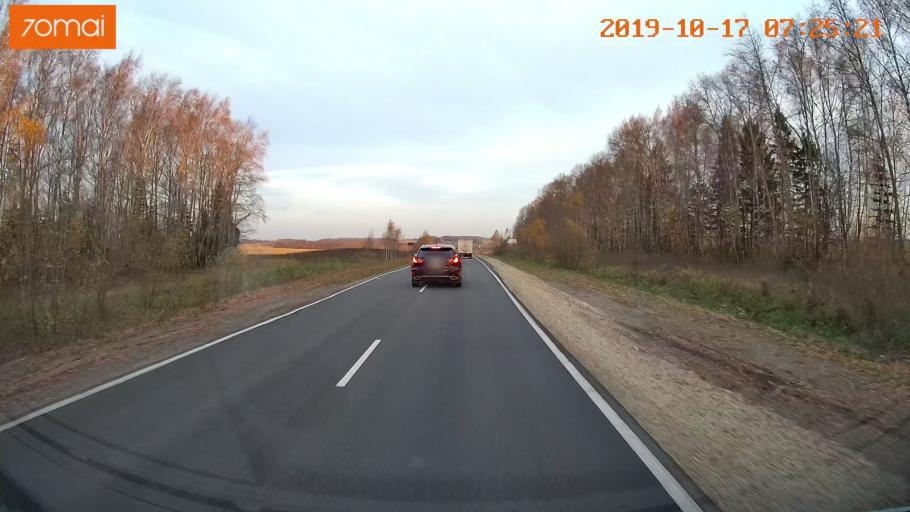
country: RU
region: Ivanovo
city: Gavrilov Posad
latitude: 56.3489
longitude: 40.1053
